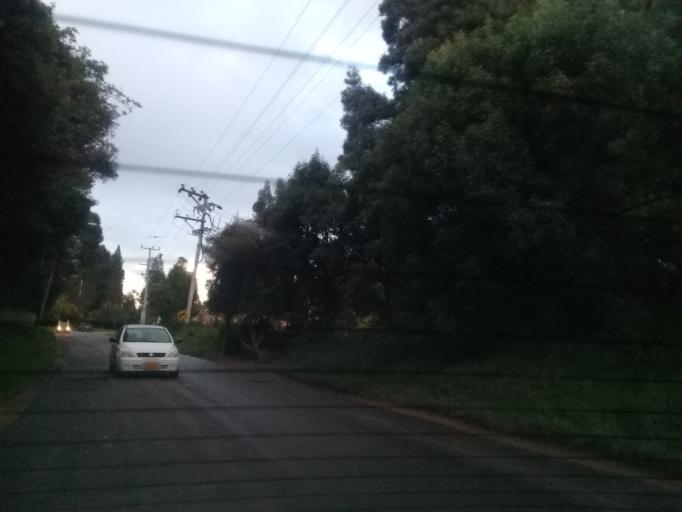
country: CO
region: Cundinamarca
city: Cajica
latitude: 4.9286
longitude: -74.0546
